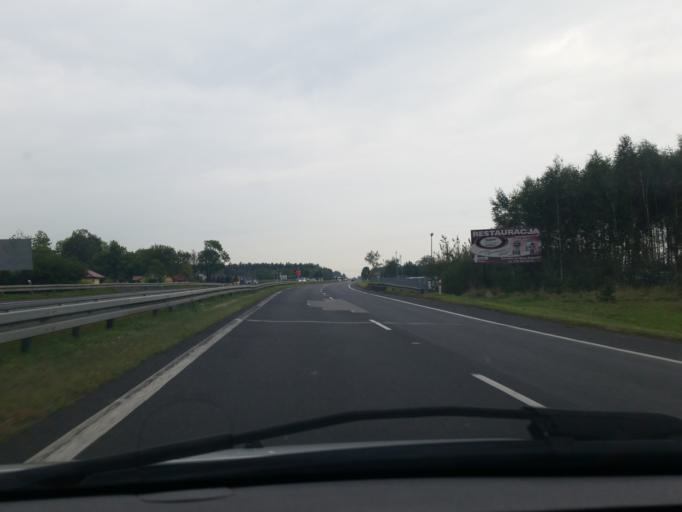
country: PL
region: Masovian Voivodeship
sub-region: Powiat zyrardowski
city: Radziejowice
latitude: 52.0046
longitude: 20.5963
